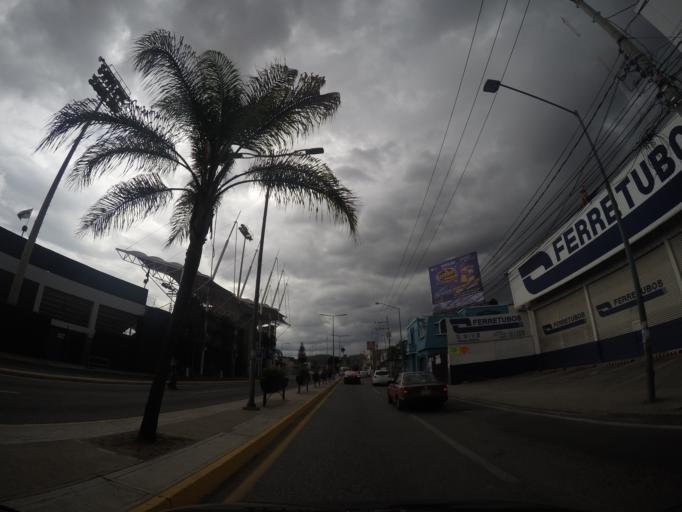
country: MX
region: Oaxaca
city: Oaxaca de Juarez
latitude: 17.0704
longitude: -96.7127
